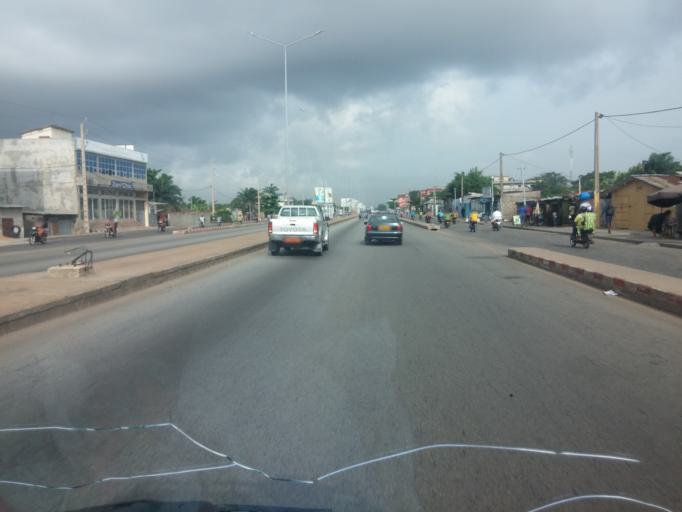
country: BJ
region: Littoral
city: Cotonou
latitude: 6.3867
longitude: 2.3710
